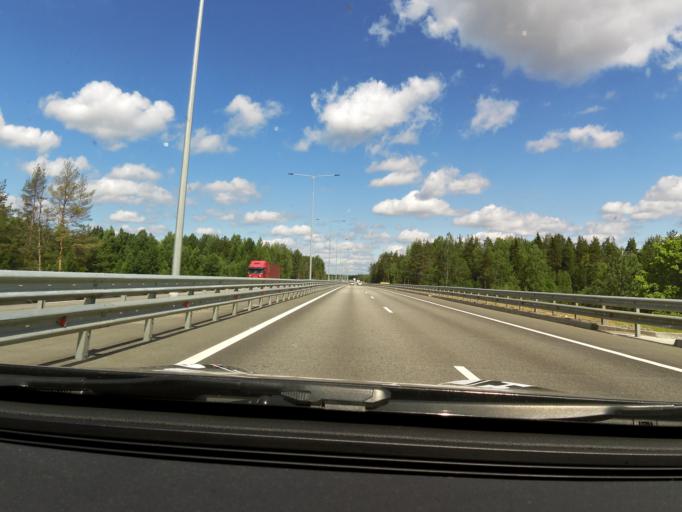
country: RU
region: Tverskaya
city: Krasnomayskiy
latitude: 57.6583
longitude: 34.2330
